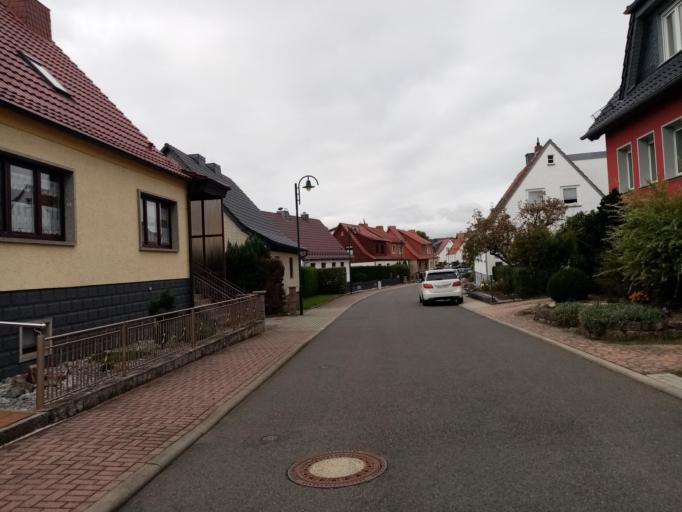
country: DE
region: Thuringia
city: Dingelstadt
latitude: 51.3225
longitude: 10.3223
